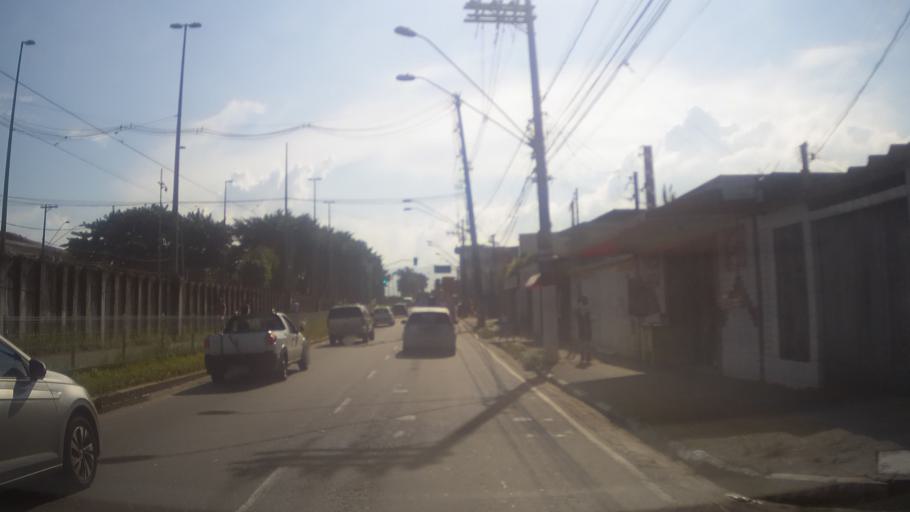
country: BR
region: Sao Paulo
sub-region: Sao Vicente
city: Sao Vicente
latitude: -23.9621
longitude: -46.3921
